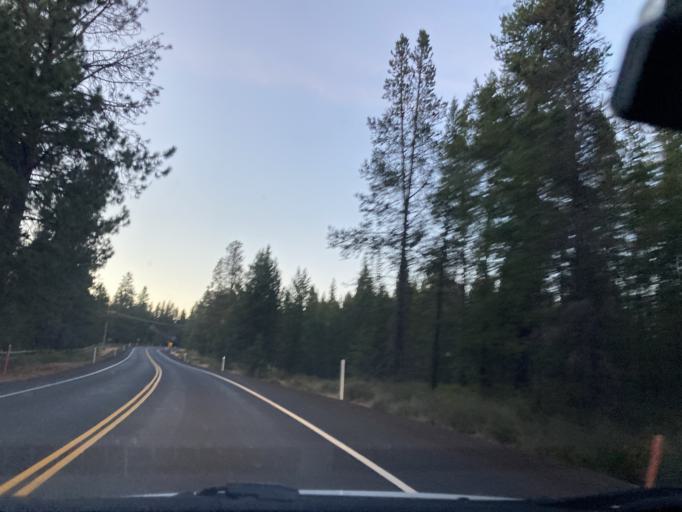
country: US
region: Oregon
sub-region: Deschutes County
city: Three Rivers
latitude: 43.8318
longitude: -121.4414
